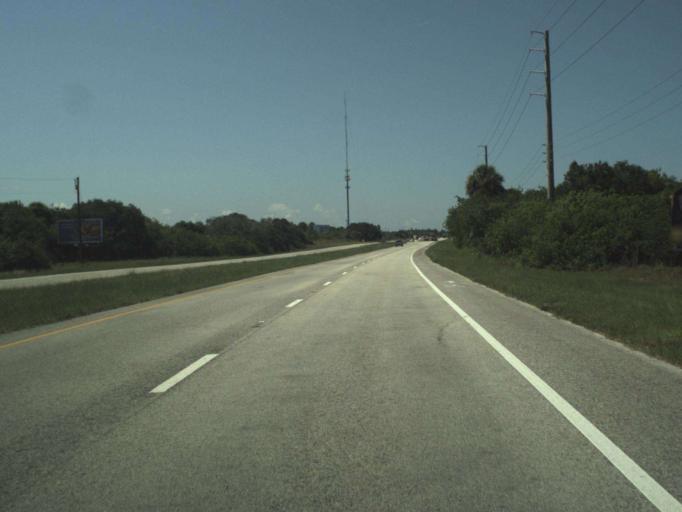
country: US
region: Florida
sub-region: Saint Lucie County
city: Lakewood Park
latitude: 27.5384
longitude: -80.3645
